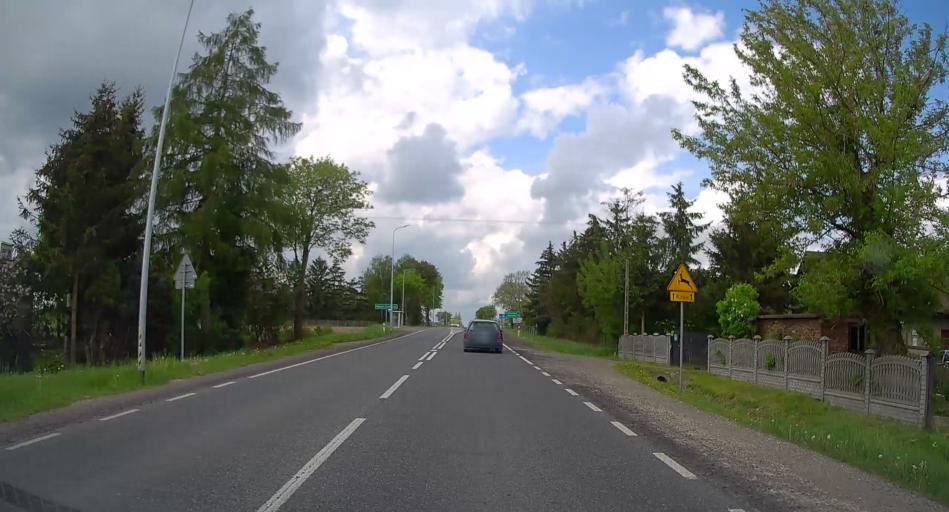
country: PL
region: Masovian Voivodeship
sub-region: Powiat plonski
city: Zaluski
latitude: 52.4441
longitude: 20.5259
